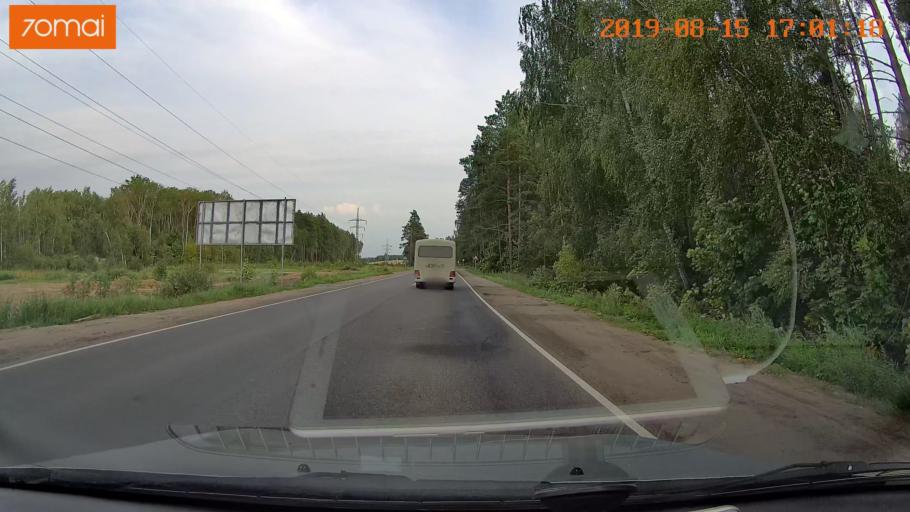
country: RU
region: Moskovskaya
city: Malyshevo
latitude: 55.4910
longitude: 38.3744
